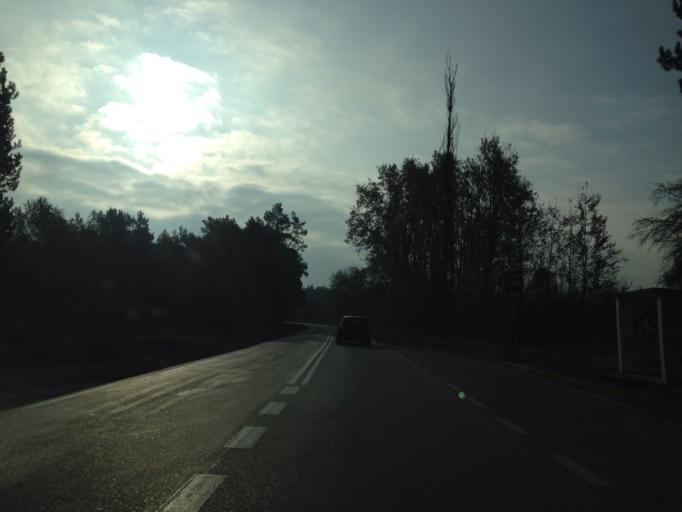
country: PL
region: Masovian Voivodeship
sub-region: Powiat zurominski
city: Biezun
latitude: 52.9301
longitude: 19.8847
